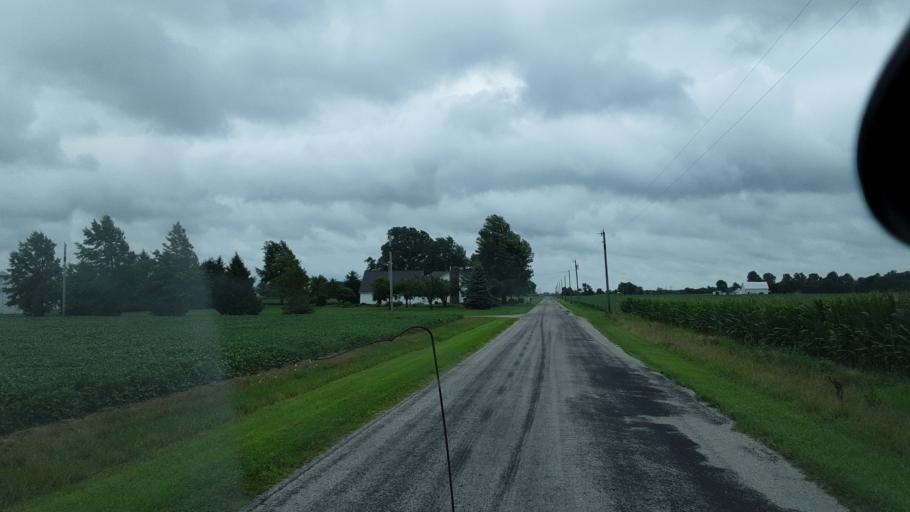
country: US
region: Indiana
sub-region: Wells County
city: Bluffton
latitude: 40.7927
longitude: -85.0715
